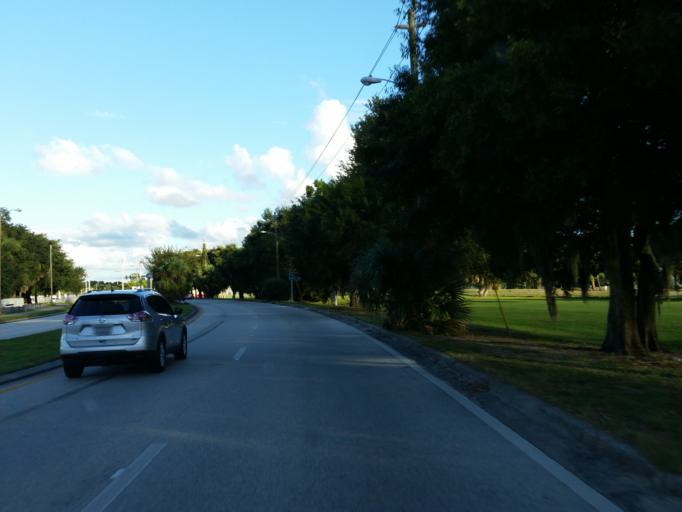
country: US
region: Florida
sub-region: Hillsborough County
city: Town 'n' Country
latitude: 27.9773
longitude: -82.5528
